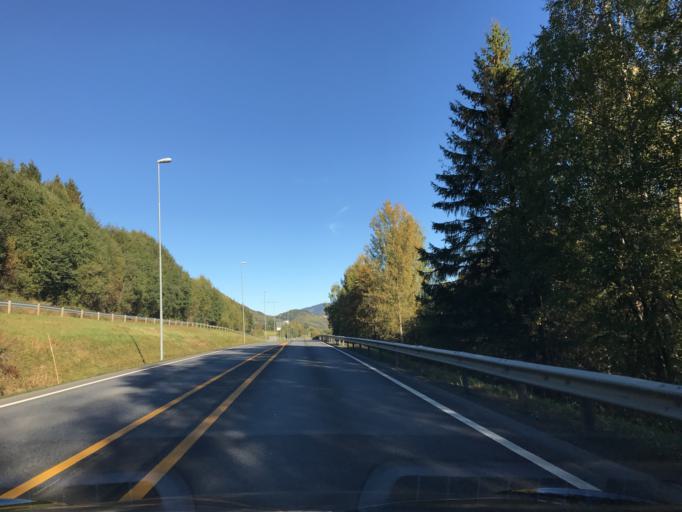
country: NO
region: Oppland
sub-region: Lillehammer
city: Lillehammer
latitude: 61.0629
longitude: 10.4307
